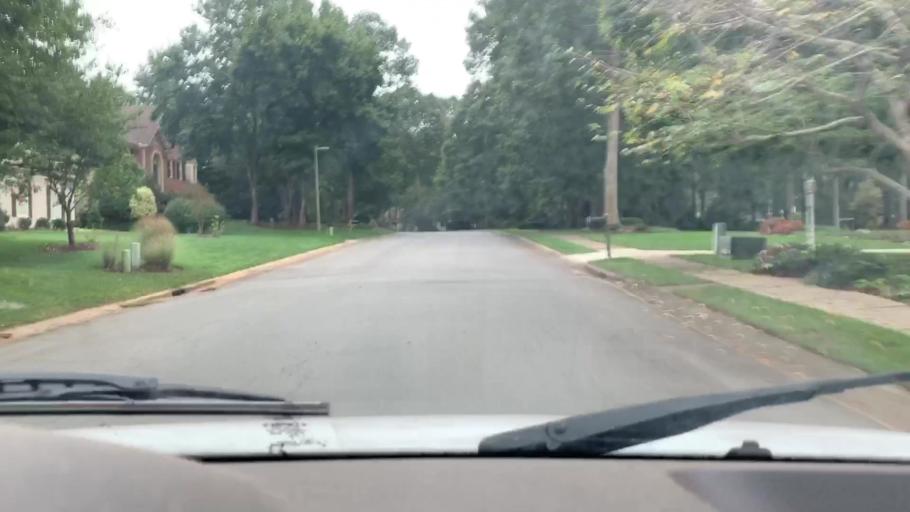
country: US
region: North Carolina
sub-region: Catawba County
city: Lake Norman of Catawba
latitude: 35.5504
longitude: -80.9093
